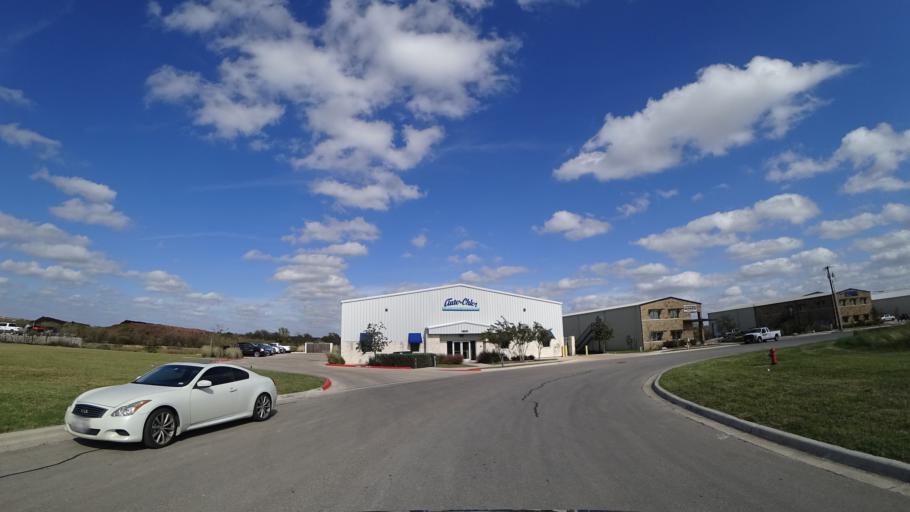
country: US
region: Texas
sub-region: Travis County
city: Windemere
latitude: 30.4708
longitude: -97.6644
